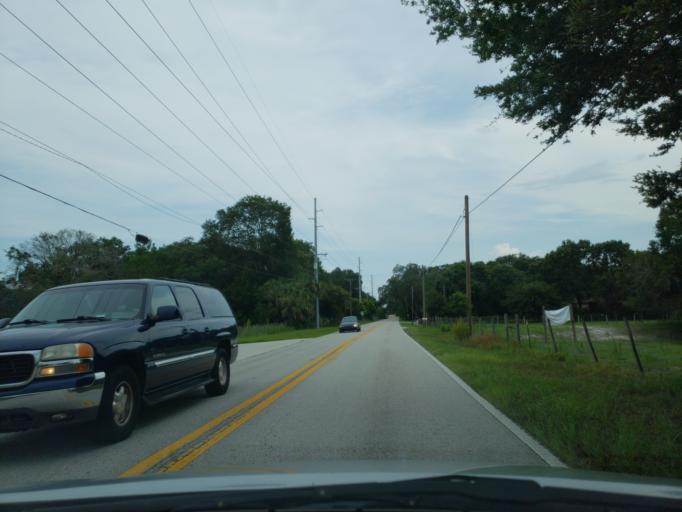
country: US
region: Florida
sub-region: Hillsborough County
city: University
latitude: 28.1140
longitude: -82.4306
